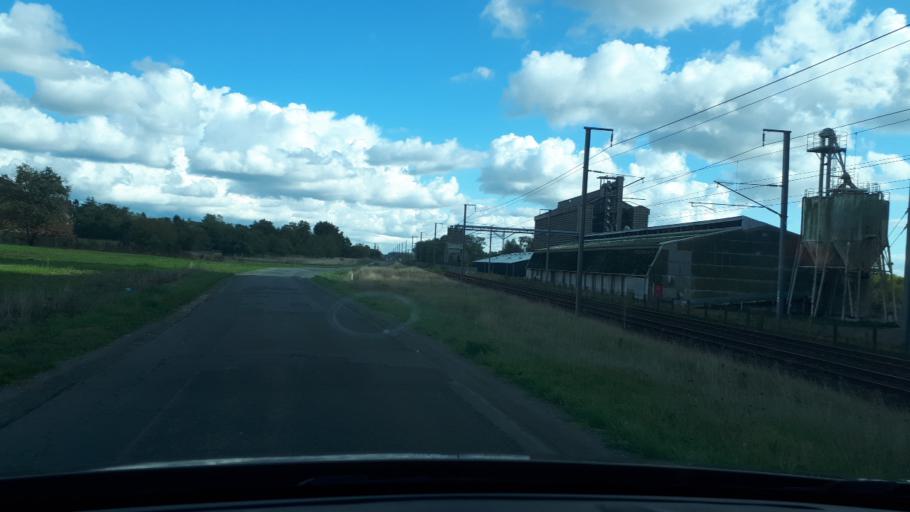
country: FR
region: Centre
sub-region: Departement du Loir-et-Cher
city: Saint-Aignan
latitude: 47.2963
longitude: 1.3633
